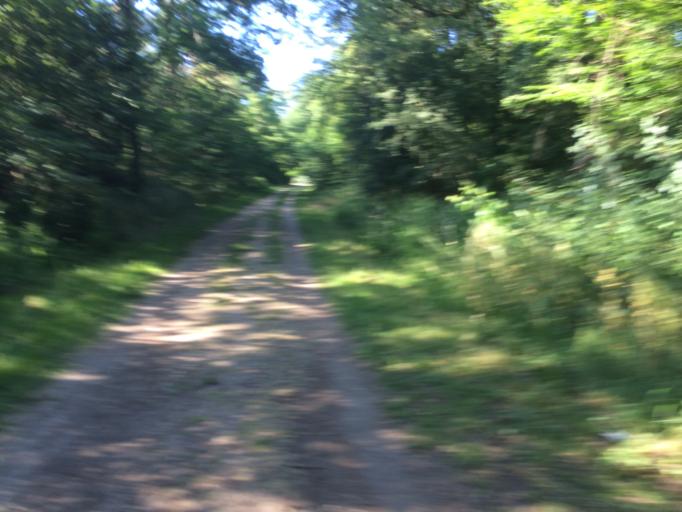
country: FR
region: Ile-de-France
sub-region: Departement du Val-de-Marne
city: Boissy-Saint-Leger
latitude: 48.7462
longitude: 2.5151
